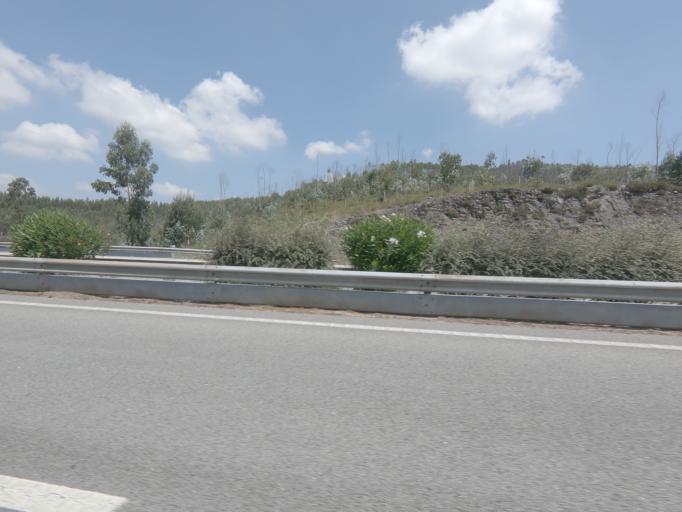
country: PT
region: Porto
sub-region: Paredes
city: Recarei
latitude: 41.1744
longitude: -8.4156
